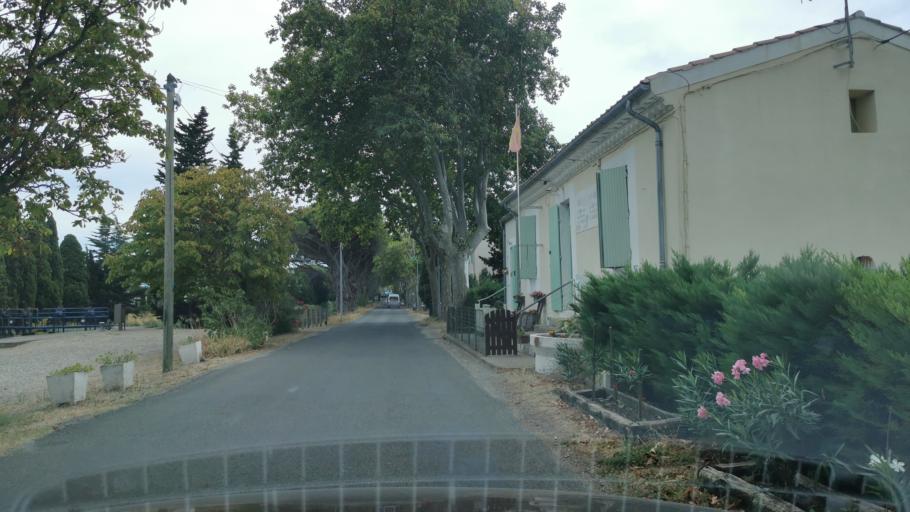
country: FR
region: Languedoc-Roussillon
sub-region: Departement de l'Aude
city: Saint-Marcel-sur-Aude
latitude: 43.2628
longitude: 2.9439
